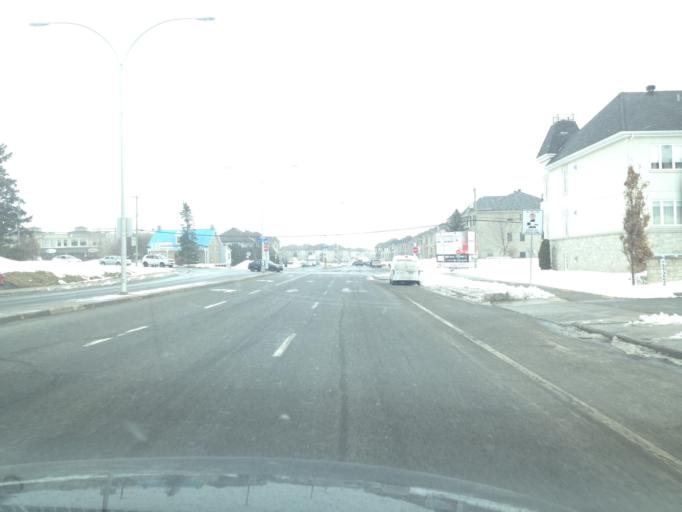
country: CA
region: Quebec
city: Dollard-Des Ormeaux
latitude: 45.5473
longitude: -73.7782
